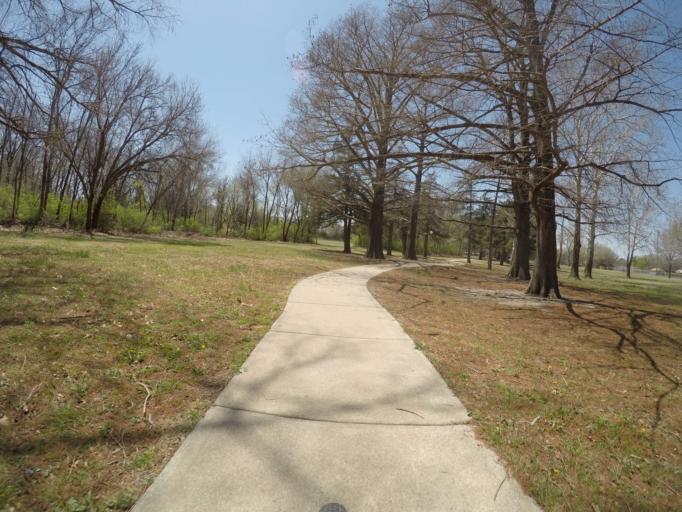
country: US
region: Kansas
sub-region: Pratt County
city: Pratt
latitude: 37.6376
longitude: -98.7319
